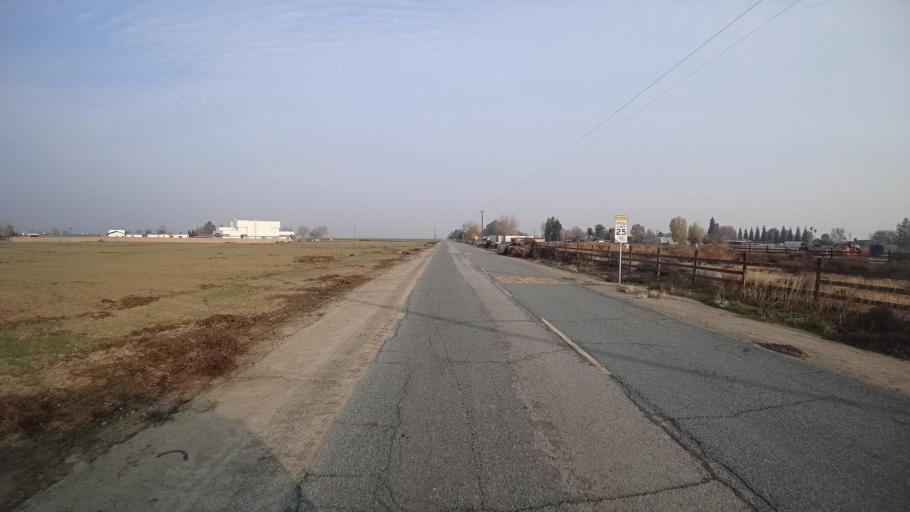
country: US
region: California
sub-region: Kern County
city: Greenfield
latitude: 35.2204
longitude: -119.0216
